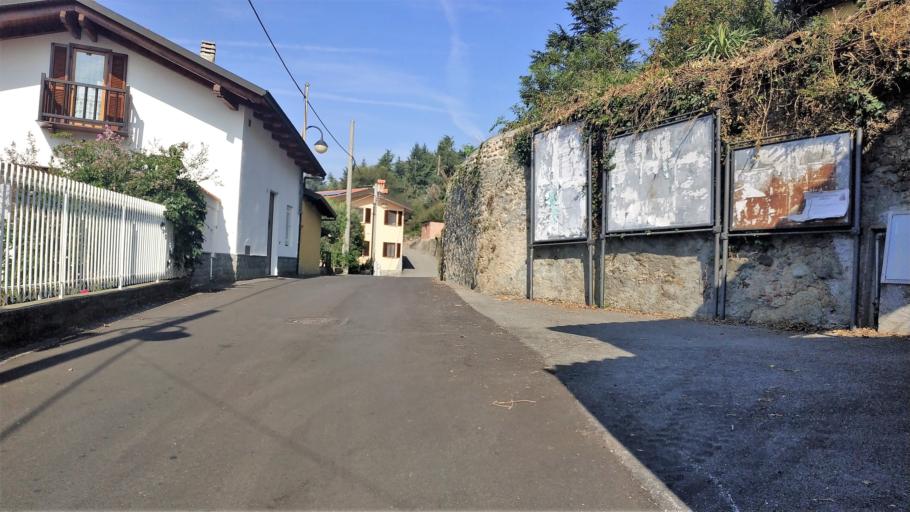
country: IT
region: Piedmont
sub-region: Provincia di Torino
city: Orio Canavese
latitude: 45.3312
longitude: 7.8594
